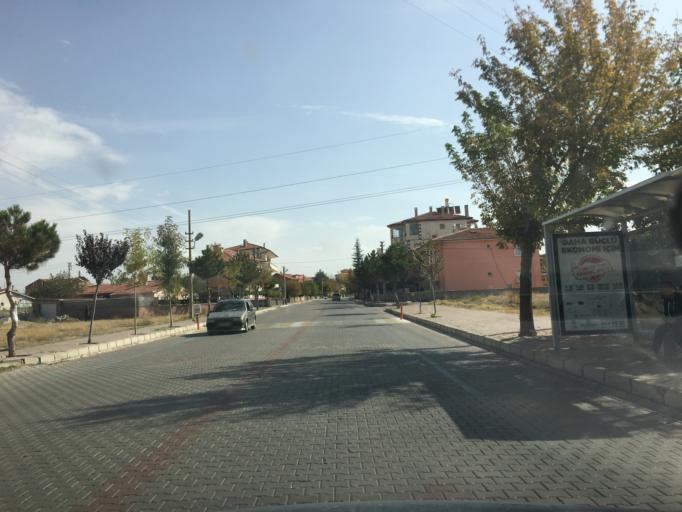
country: TR
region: Nevsehir
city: Avanos
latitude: 38.7103
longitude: 34.8483
